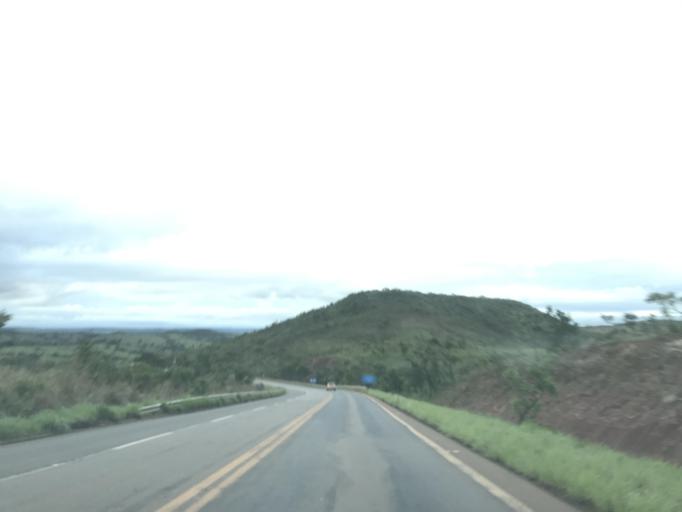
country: BR
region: Goias
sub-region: Luziania
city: Luziania
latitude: -16.3975
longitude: -48.1104
